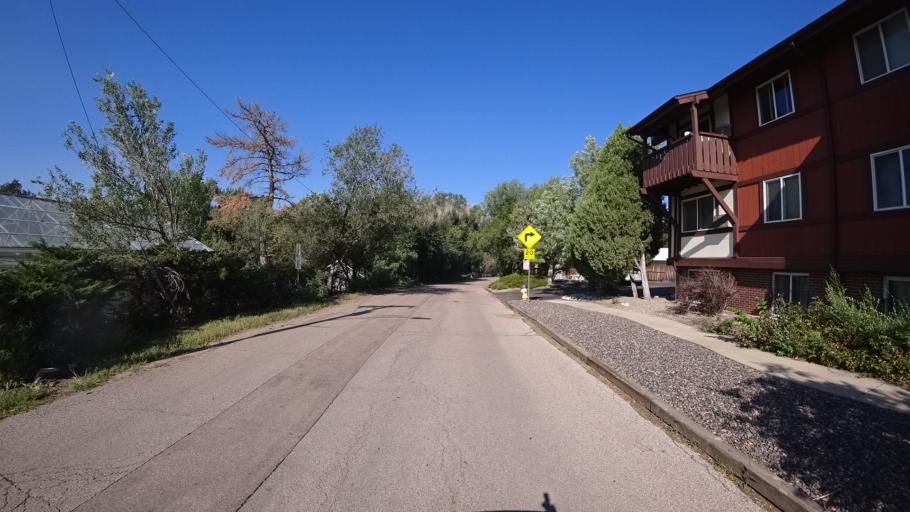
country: US
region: Colorado
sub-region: El Paso County
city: Colorado Springs
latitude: 38.8678
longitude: -104.8256
